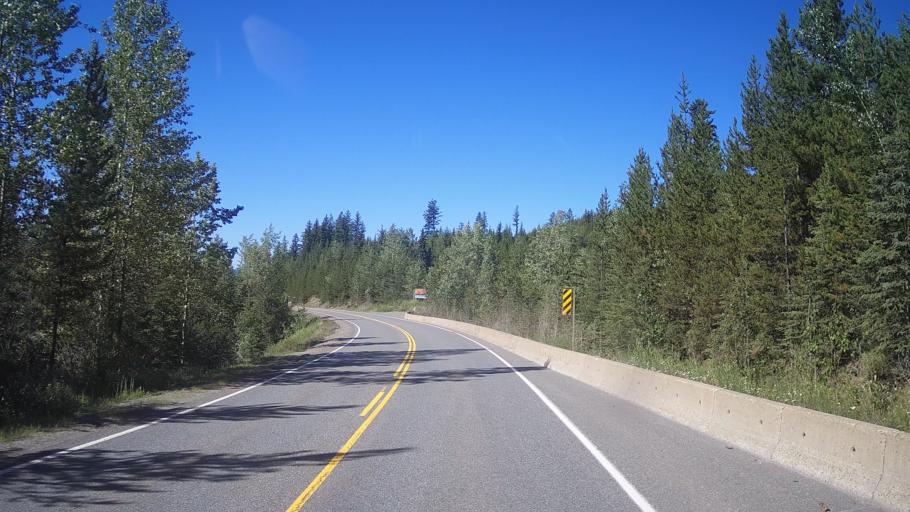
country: CA
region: British Columbia
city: Kamloops
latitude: 51.4972
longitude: -120.4497
